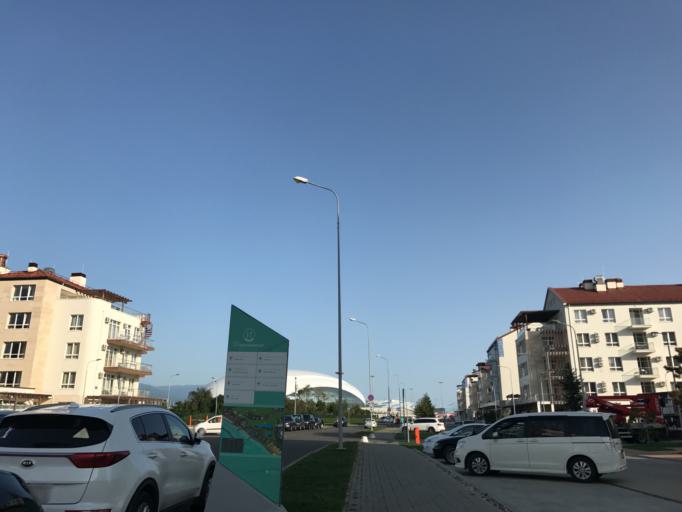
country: RU
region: Krasnodarskiy
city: Adler
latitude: 43.4070
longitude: 39.9432
